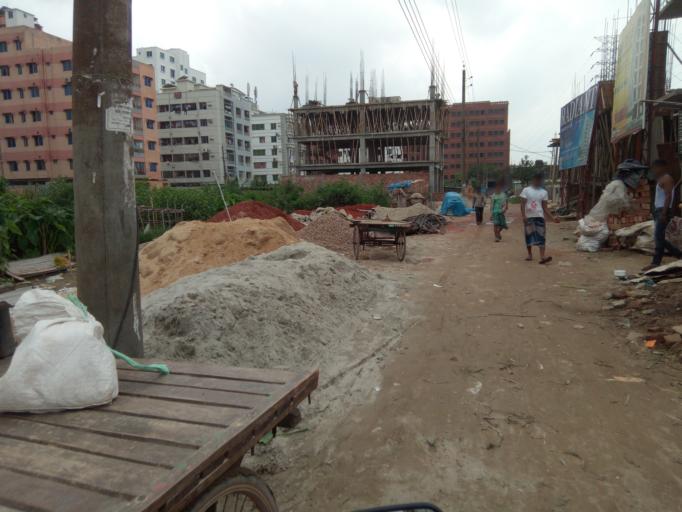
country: BD
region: Dhaka
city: Paltan
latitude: 23.7680
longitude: 90.4276
